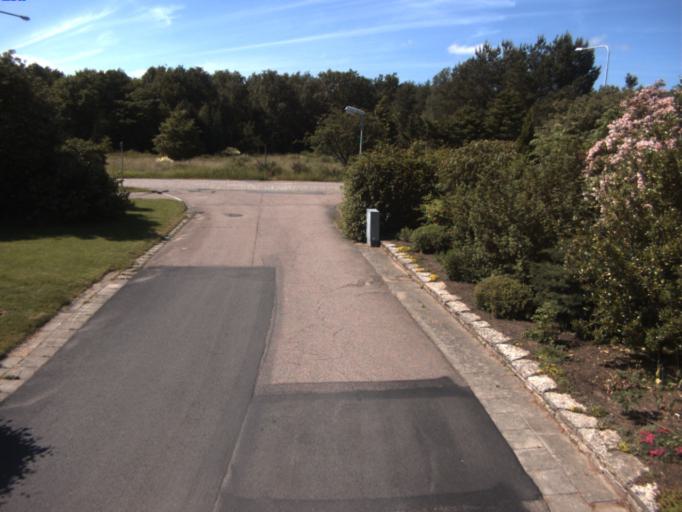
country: SE
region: Skane
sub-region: Helsingborg
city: Odakra
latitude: 56.0733
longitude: 12.7331
